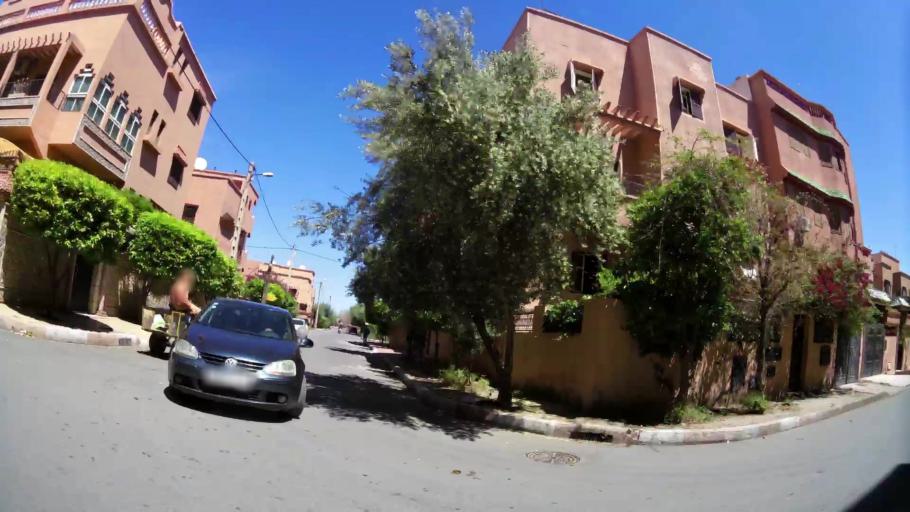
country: MA
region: Marrakech-Tensift-Al Haouz
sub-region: Marrakech
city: Marrakesh
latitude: 31.6374
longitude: -8.0603
